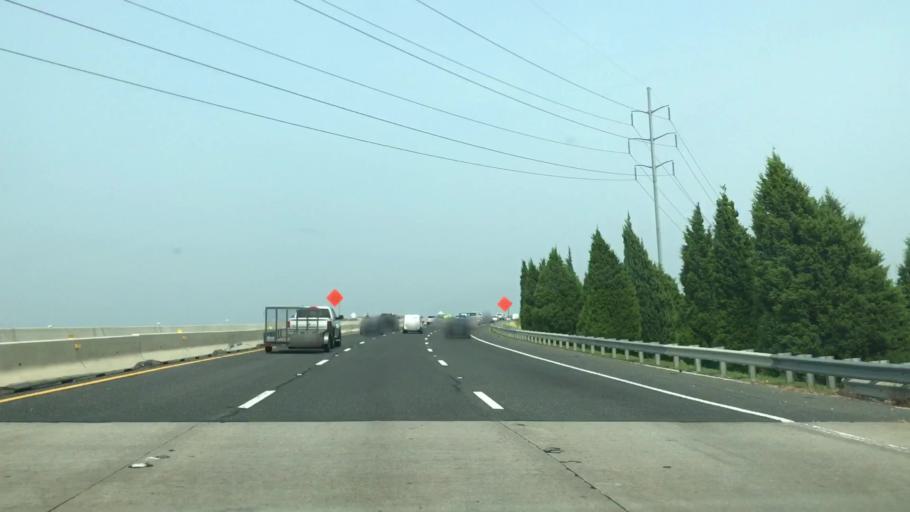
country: US
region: Texas
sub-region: Dallas County
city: Addison
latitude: 33.0116
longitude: -96.8483
